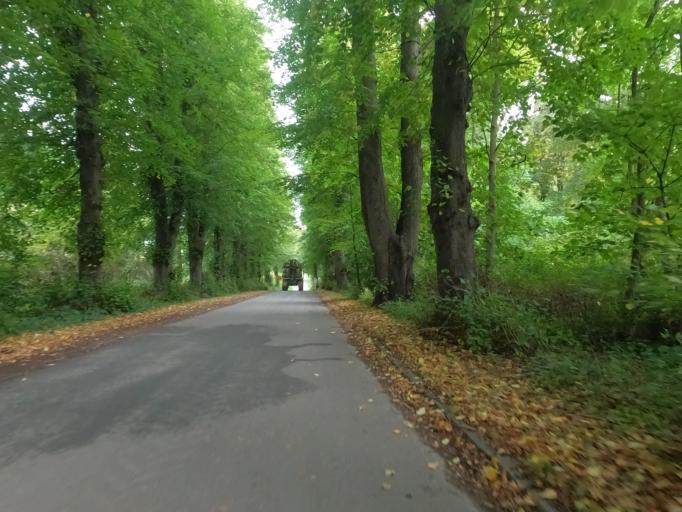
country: DE
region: Schleswig-Holstein
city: Neukirchen
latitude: 54.2902
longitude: 11.0577
